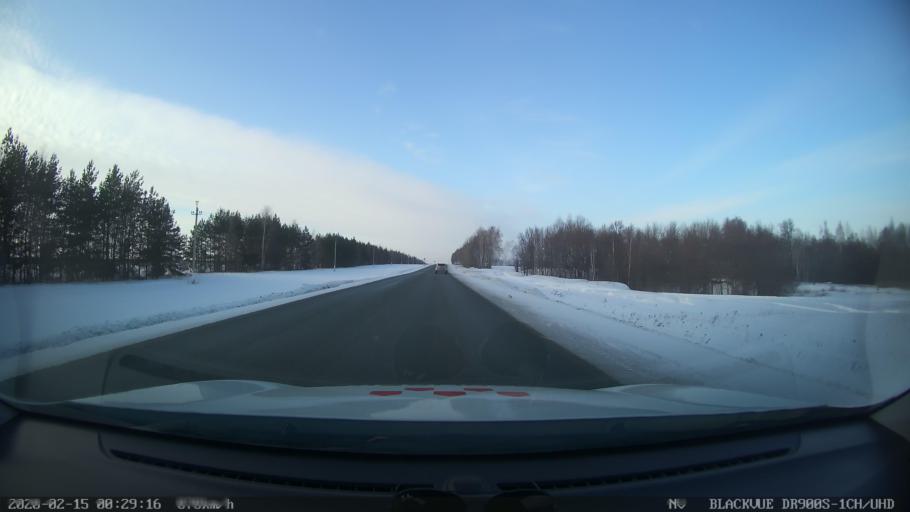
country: RU
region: Tatarstan
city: Verkhniy Uslon
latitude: 55.6493
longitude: 48.8701
